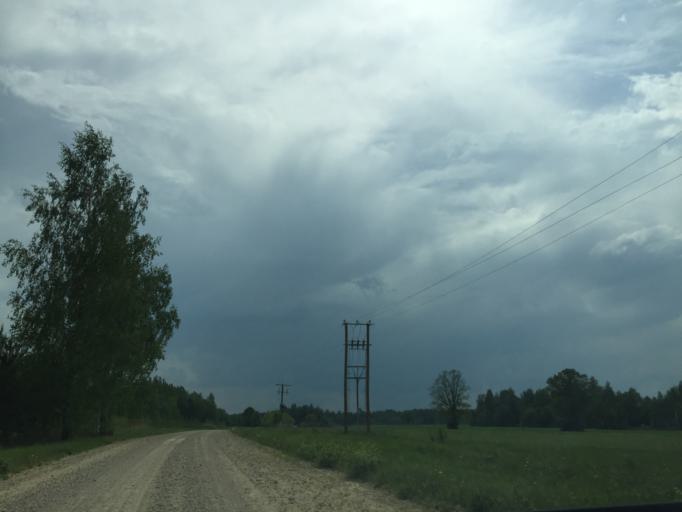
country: LV
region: Livani
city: Livani
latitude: 56.5749
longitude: 26.2172
